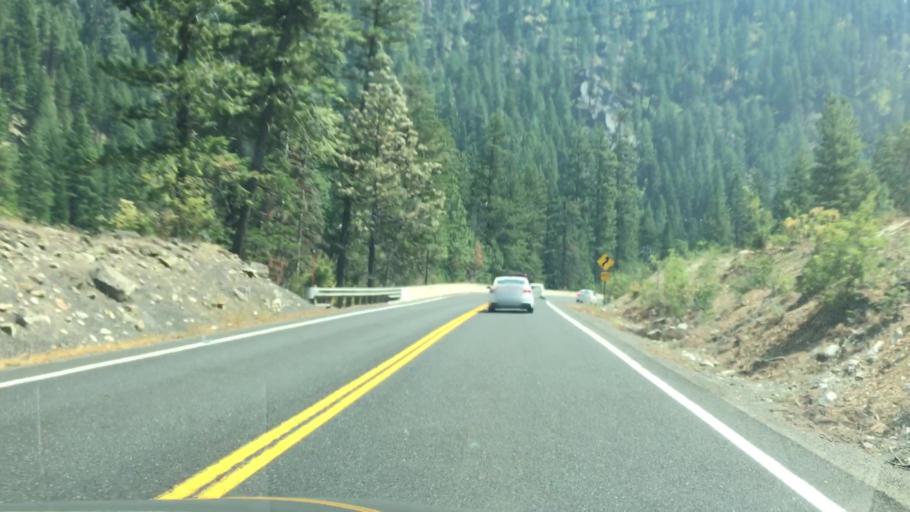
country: US
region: Idaho
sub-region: Valley County
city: McCall
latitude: 45.1475
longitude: -116.2899
